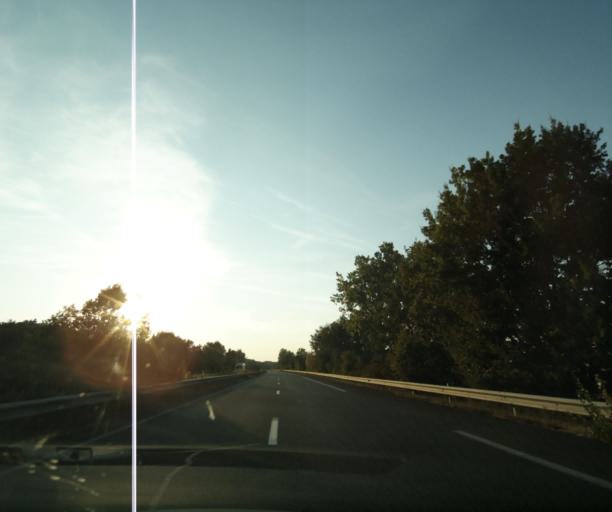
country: FR
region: Aquitaine
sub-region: Departement du Lot-et-Garonne
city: Layrac
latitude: 44.1229
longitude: 0.7102
